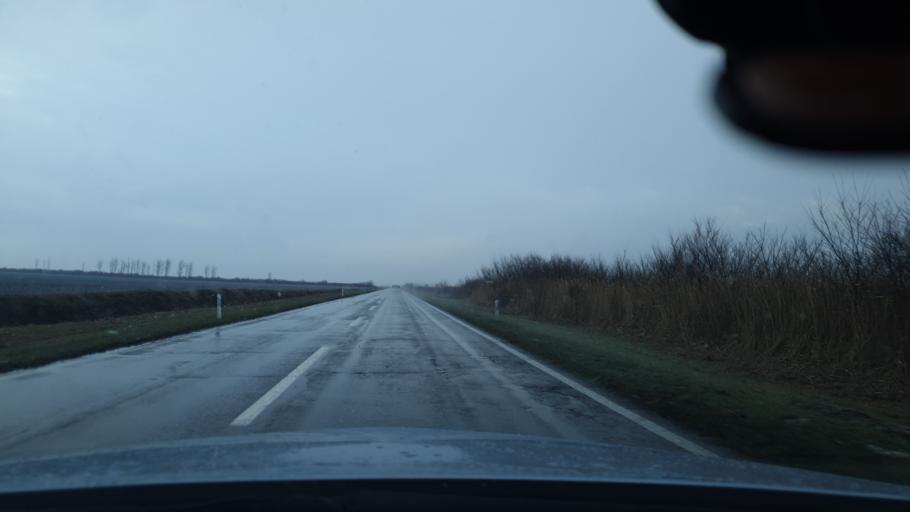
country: RS
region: Autonomna Pokrajina Vojvodina
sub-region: Juznobanatski Okrug
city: Pancevo
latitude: 44.8518
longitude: 20.7678
